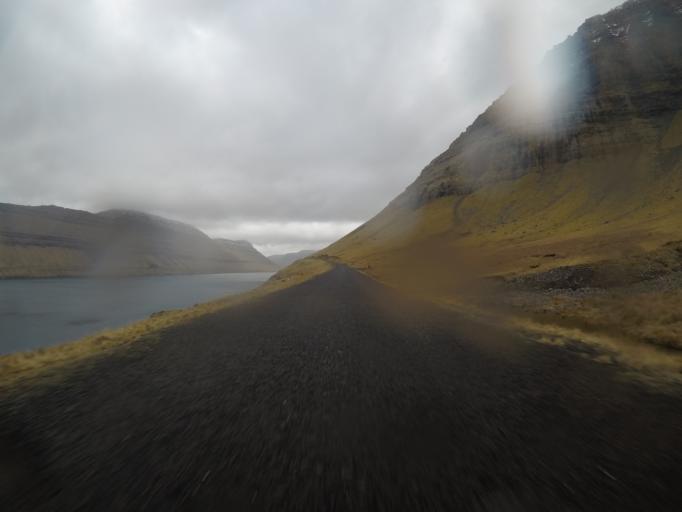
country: FO
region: Nordoyar
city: Klaksvik
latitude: 62.3333
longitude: -6.5755
